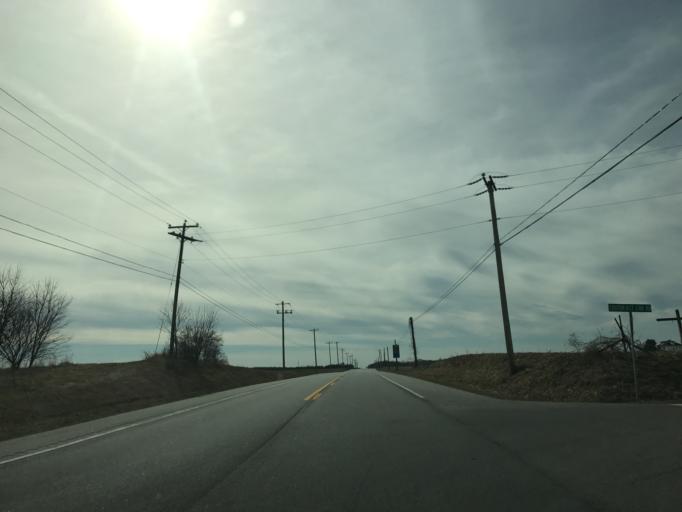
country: US
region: Maryland
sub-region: Queen Anne's County
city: Kingstown
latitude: 39.1366
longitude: -75.9946
